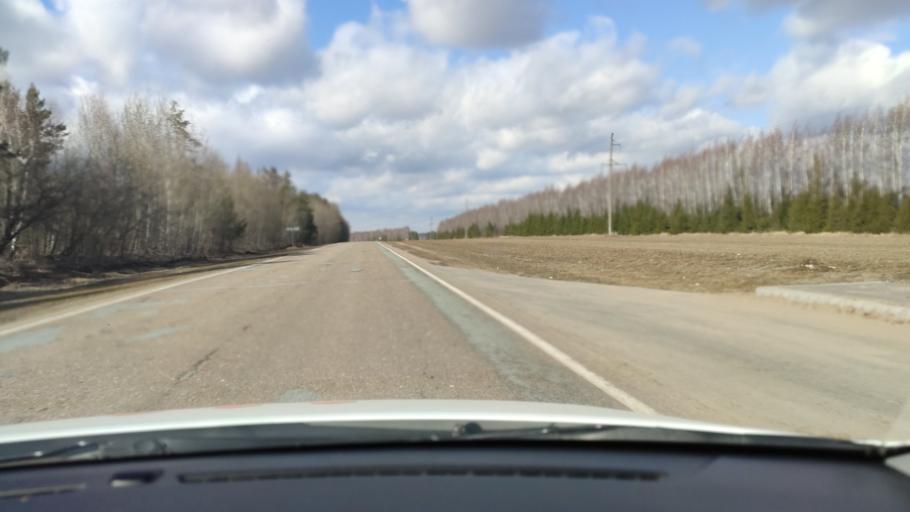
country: RU
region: Tatarstan
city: Vysokaya Gora
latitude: 56.0669
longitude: 49.1999
